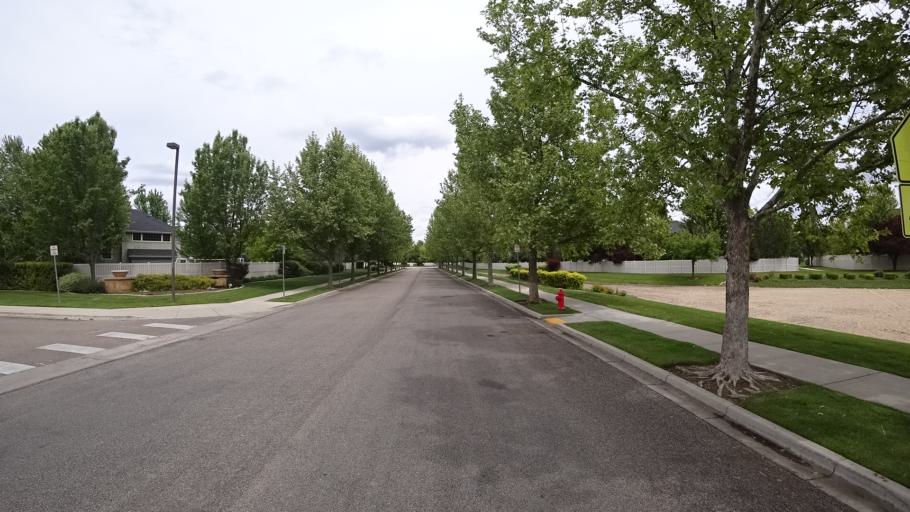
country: US
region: Idaho
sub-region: Ada County
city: Meridian
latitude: 43.6440
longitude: -116.4238
